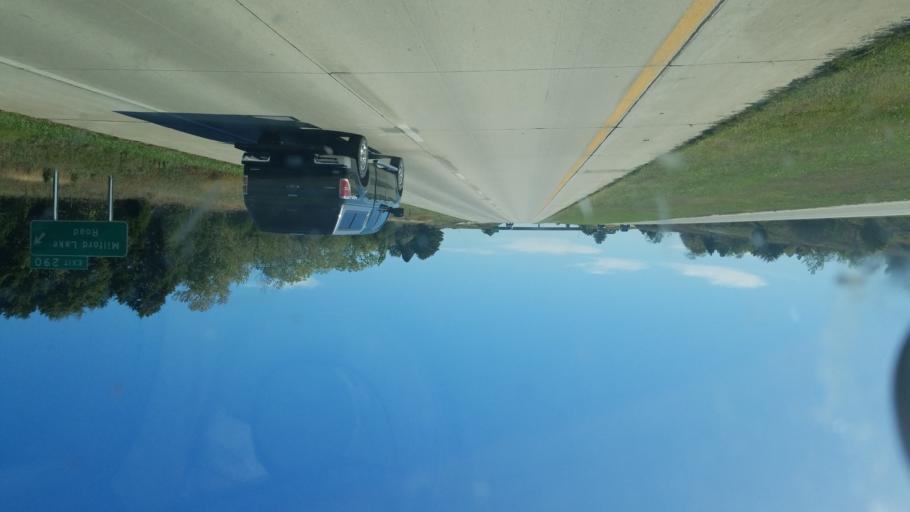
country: US
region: Kansas
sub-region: Dickinson County
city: Chapman
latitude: 38.9981
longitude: -96.9388
